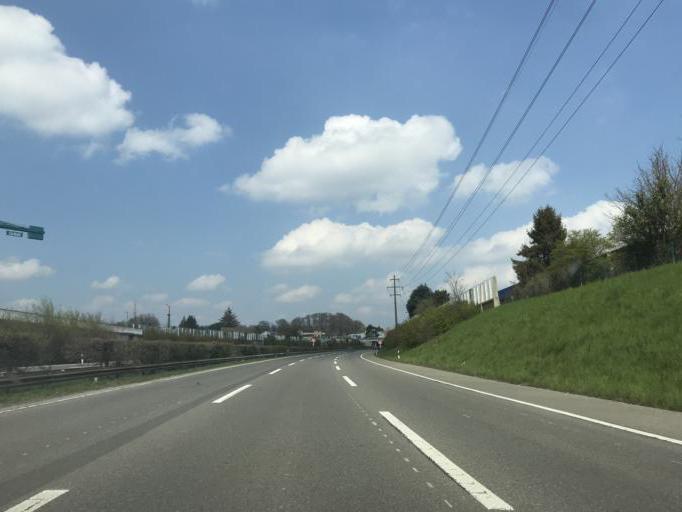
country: CH
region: Vaud
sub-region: Ouest Lausannois District
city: Chavannes
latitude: 46.5310
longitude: 6.5734
